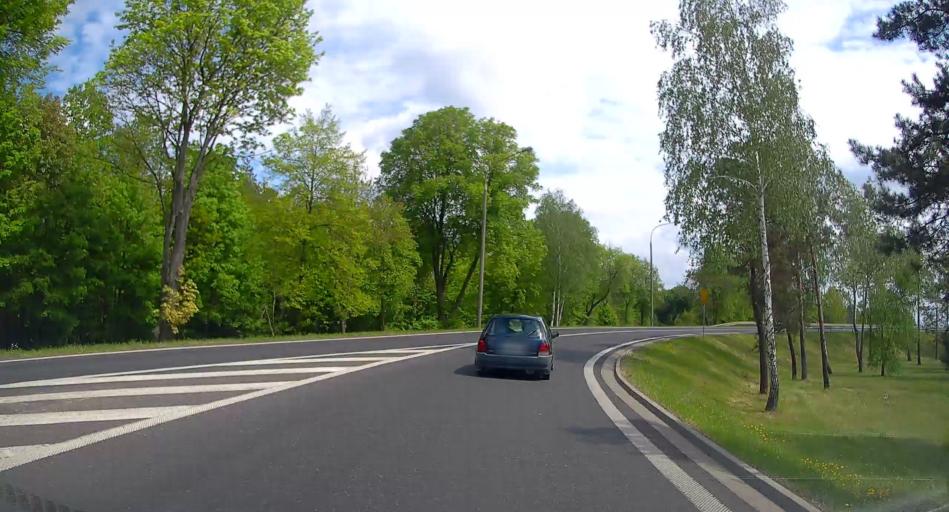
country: PL
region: Masovian Voivodeship
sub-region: Powiat nowodworski
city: Zakroczym
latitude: 52.4412
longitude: 20.6406
